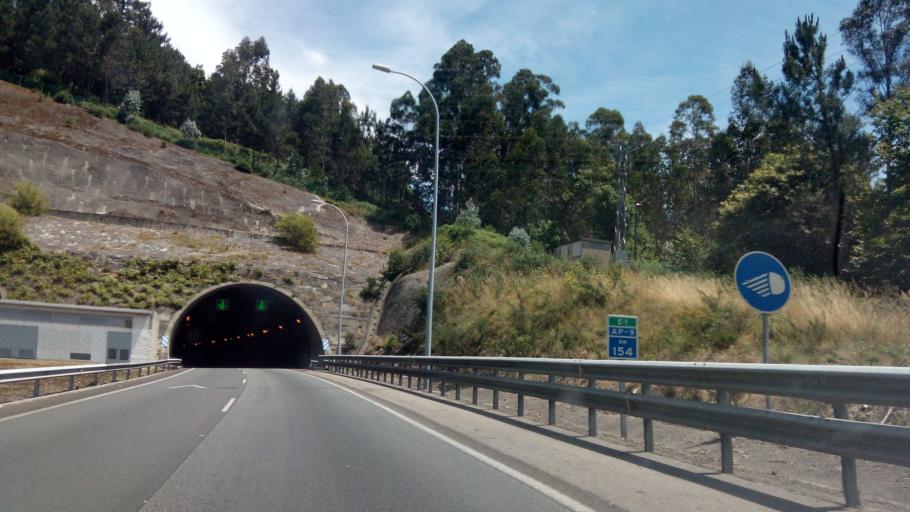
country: ES
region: Galicia
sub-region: Provincia de Pontevedra
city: Vigo
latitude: 42.2397
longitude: -8.6765
